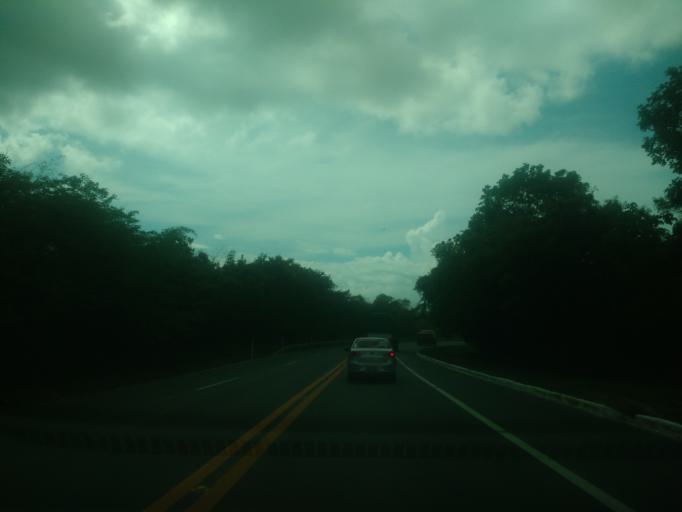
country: BR
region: Alagoas
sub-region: Marechal Deodoro
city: Marechal Deodoro
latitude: -9.6890
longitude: -35.8175
